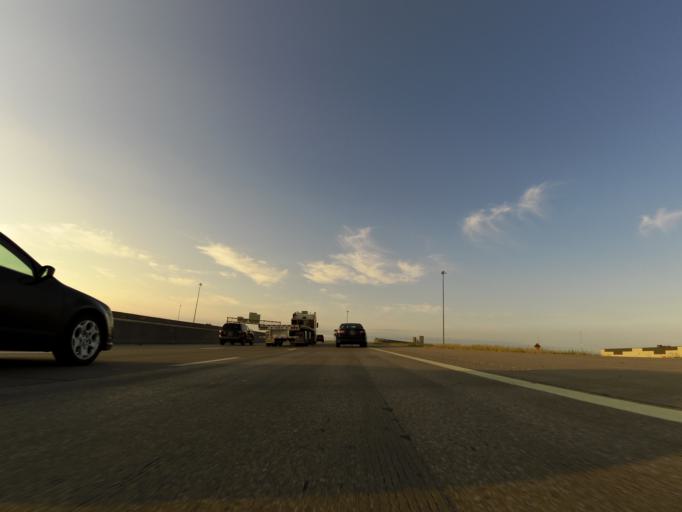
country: US
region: Kansas
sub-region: Sedgwick County
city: Wichita
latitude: 37.7414
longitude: -97.3193
